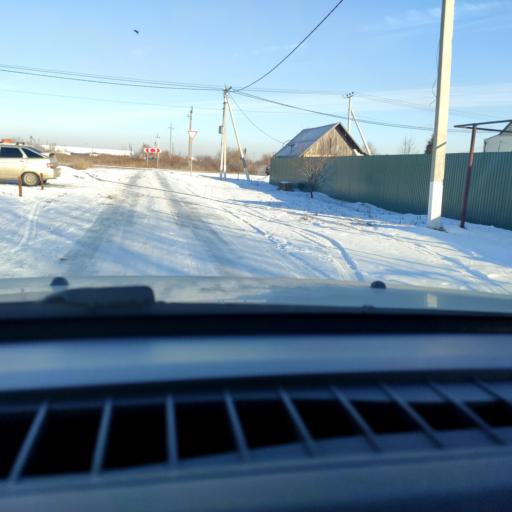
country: RU
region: Samara
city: Podstepki
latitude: 53.5185
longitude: 49.1283
